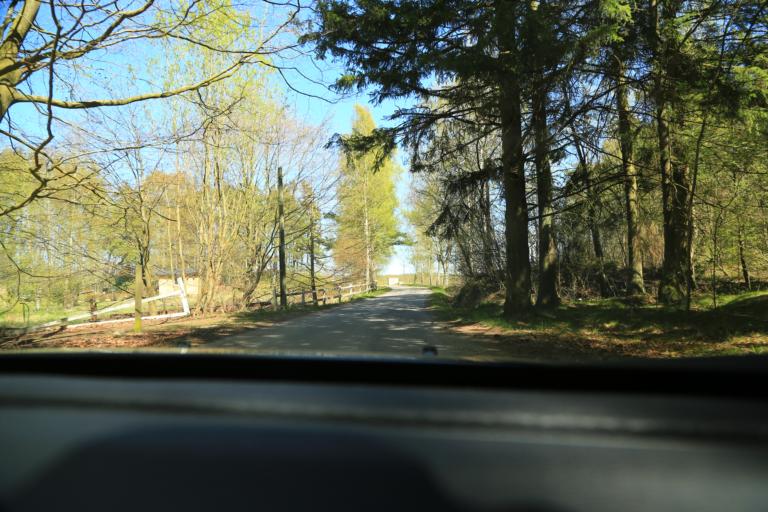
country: SE
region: Halland
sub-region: Varbergs Kommun
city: Traslovslage
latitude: 57.0940
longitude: 12.2900
